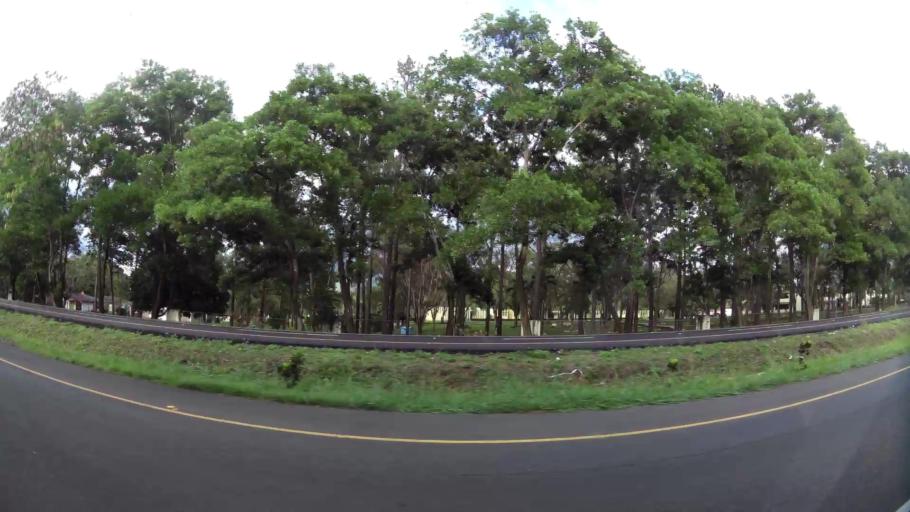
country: DO
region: Monsenor Nouel
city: Piedra Blanca
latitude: 18.8673
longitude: -70.3577
